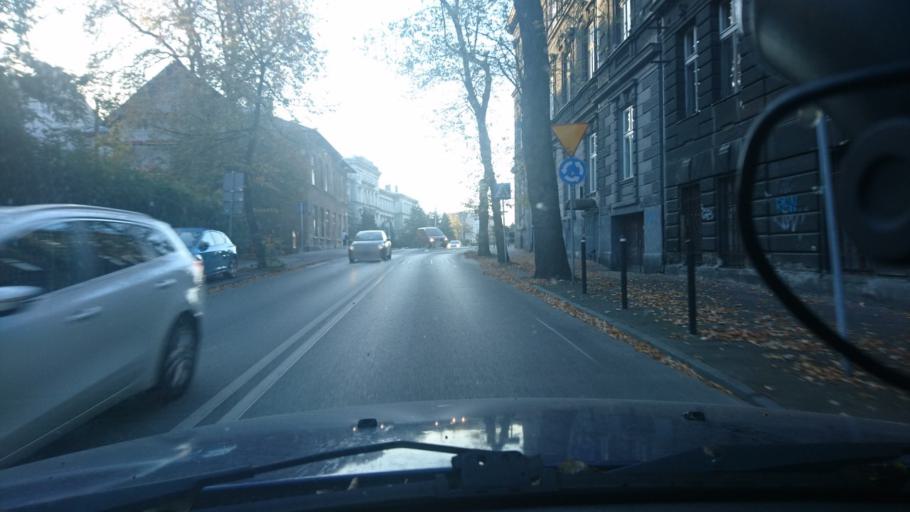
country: PL
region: Silesian Voivodeship
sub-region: Bielsko-Biala
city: Bielsko-Biala
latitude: 49.8259
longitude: 19.0404
